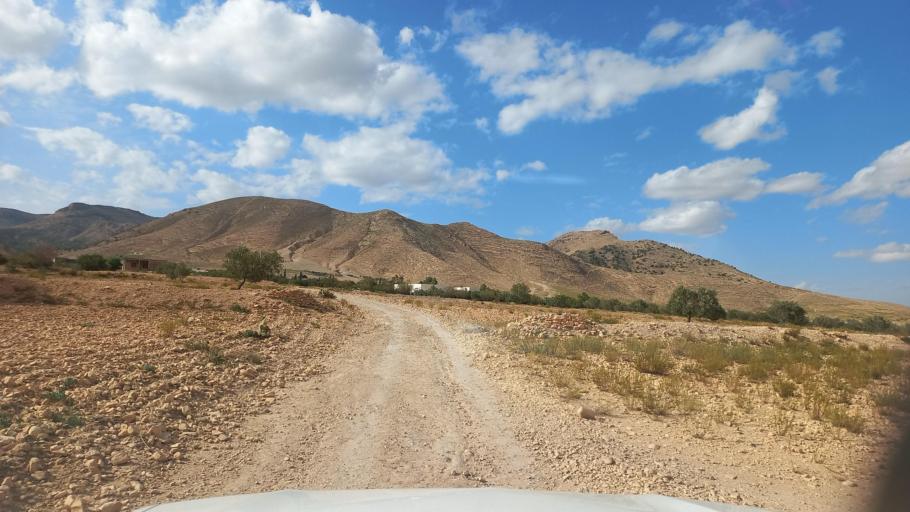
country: TN
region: Al Qasrayn
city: Sbiba
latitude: 35.4498
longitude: 9.0753
